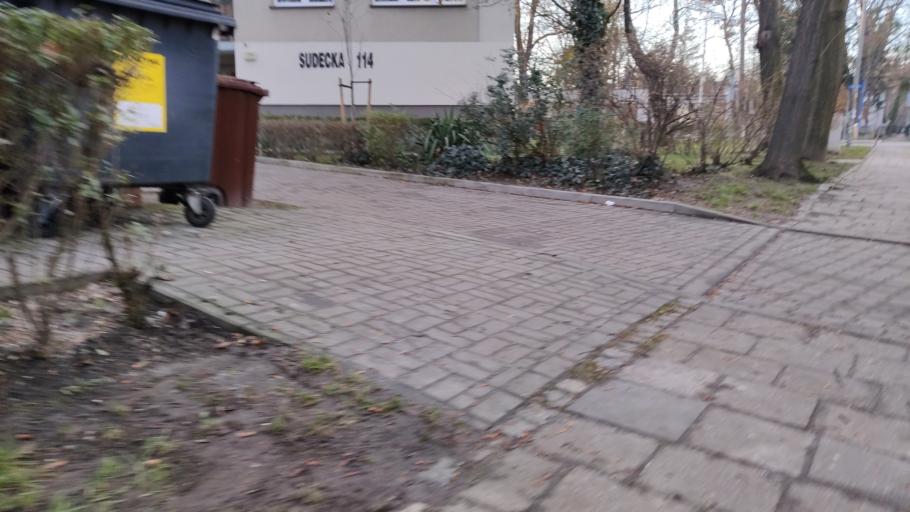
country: PL
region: Lower Silesian Voivodeship
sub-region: Powiat wroclawski
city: Wroclaw
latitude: 51.0815
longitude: 17.0173
